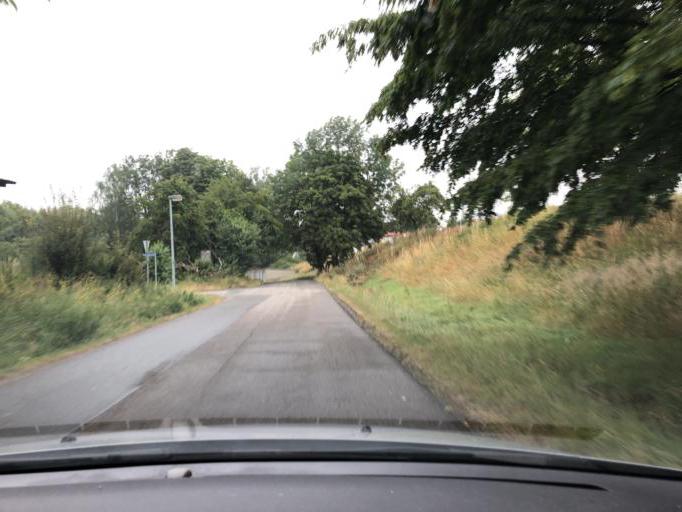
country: DE
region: Thuringia
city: Langenleuba-Niederhain
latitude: 51.0120
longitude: 12.6131
